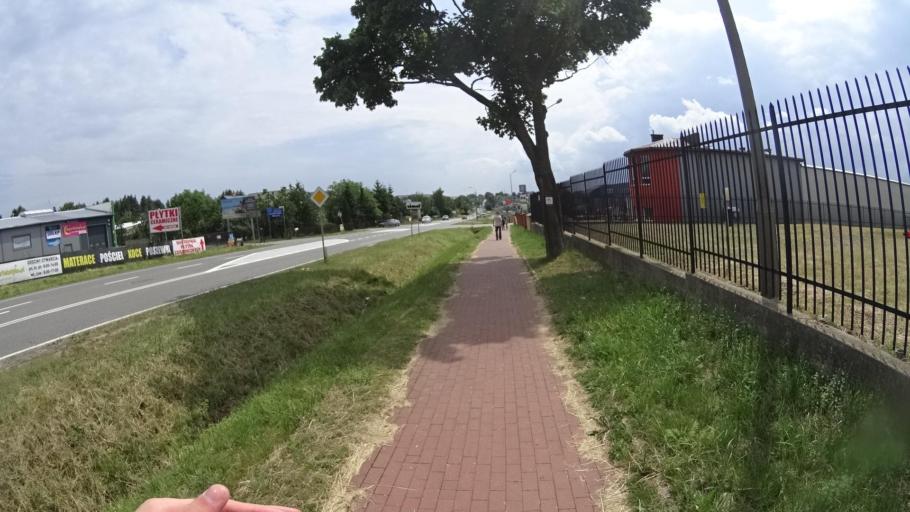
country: PL
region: Masovian Voivodeship
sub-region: Powiat grojecki
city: Grojec
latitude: 51.8796
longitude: 20.8638
